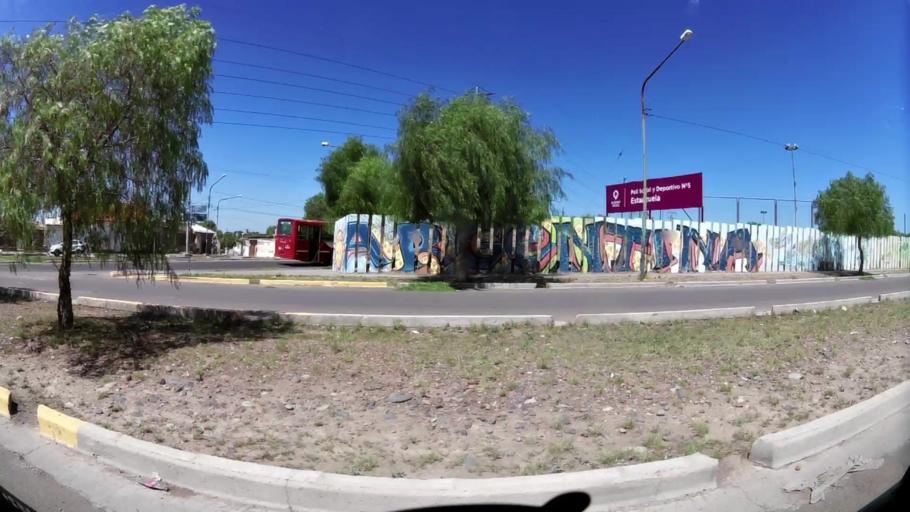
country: AR
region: Mendoza
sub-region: Departamento de Godoy Cruz
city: Godoy Cruz
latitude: -32.9419
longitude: -68.8719
